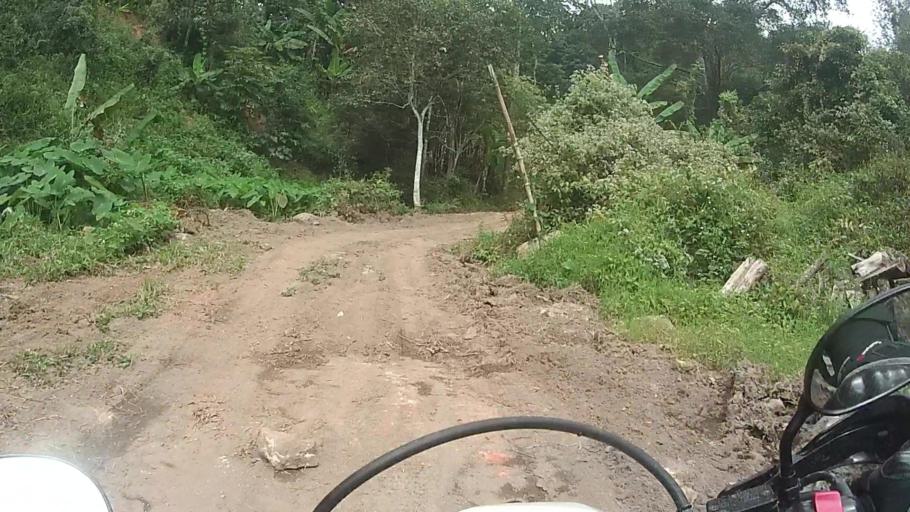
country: TH
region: Chiang Mai
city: Mae On
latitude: 18.7966
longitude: 99.3499
